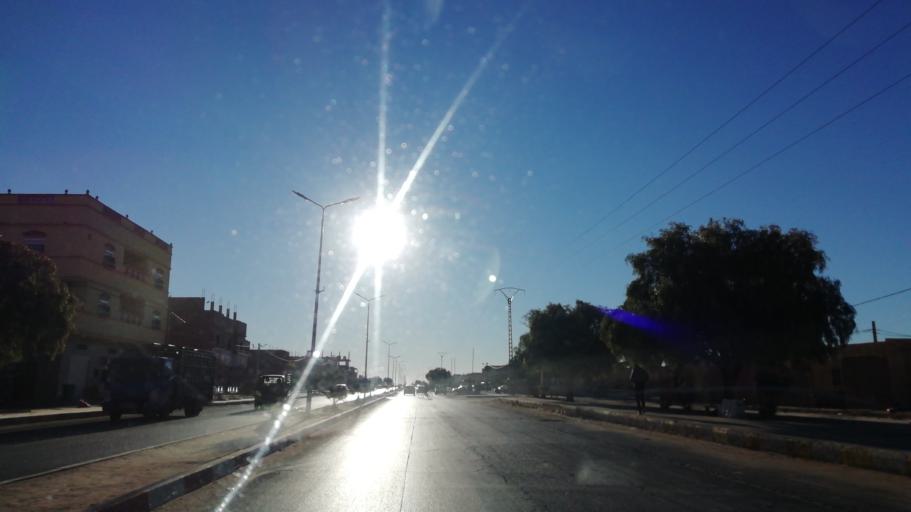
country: DZ
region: Saida
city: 'Ain el Hadjar
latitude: 34.0303
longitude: 0.0912
